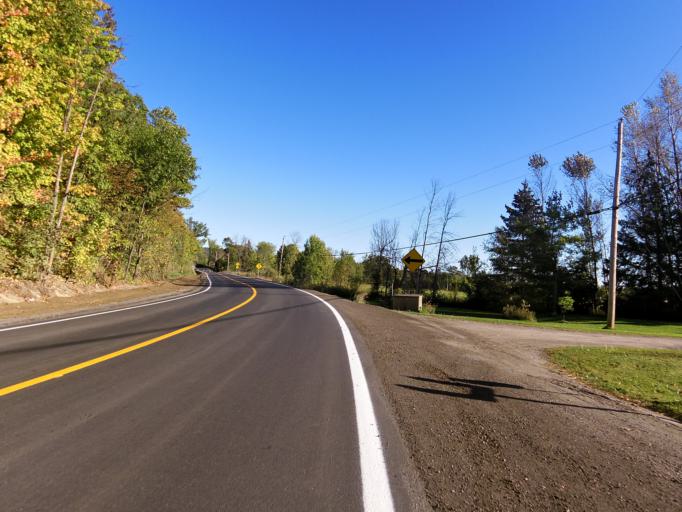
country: CA
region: Quebec
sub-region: Outaouais
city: Wakefield
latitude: 45.4917
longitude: -75.8920
